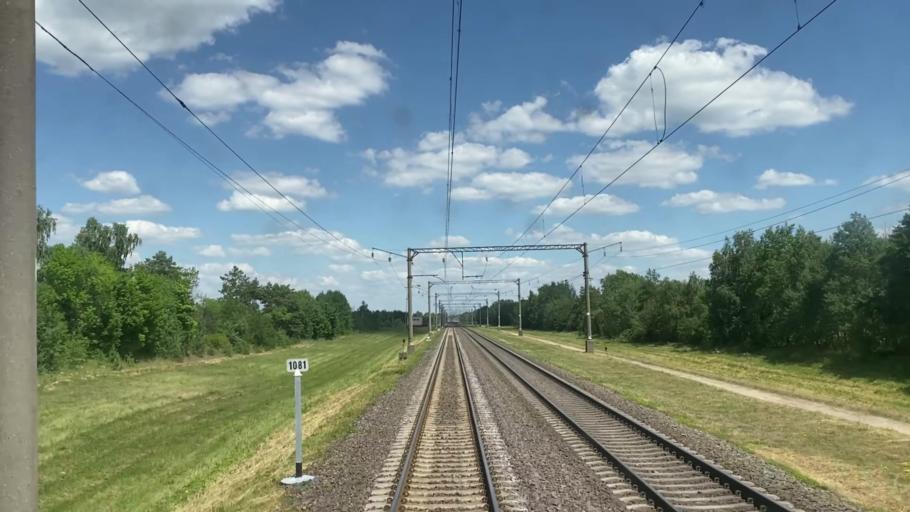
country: BY
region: Brest
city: Zhabinka
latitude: 52.1492
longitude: 23.8719
